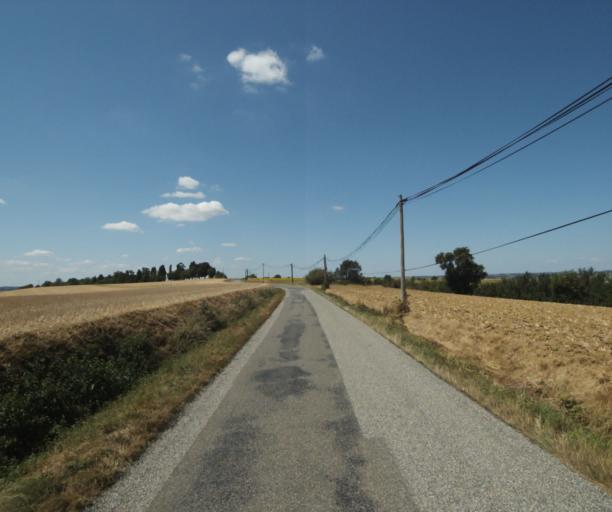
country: FR
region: Midi-Pyrenees
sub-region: Departement de la Haute-Garonne
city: Saint-Felix-Lauragais
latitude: 43.4600
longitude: 1.8807
